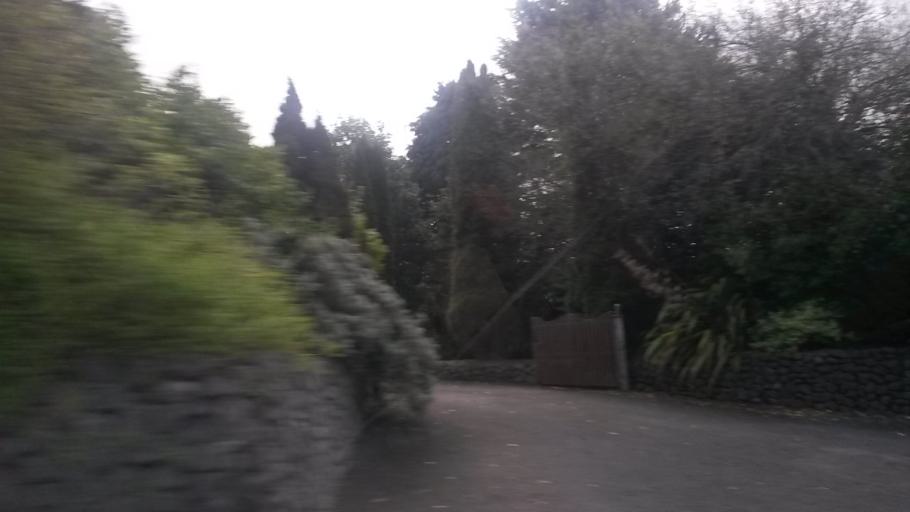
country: IE
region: Munster
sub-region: County Cork
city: Cobh
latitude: 51.8881
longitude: -8.3077
